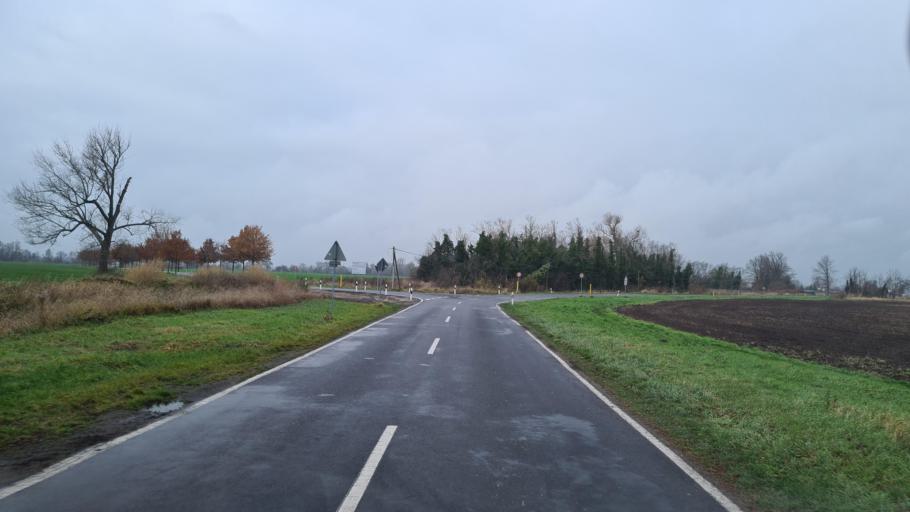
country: DE
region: Brandenburg
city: Nauen
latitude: 52.6250
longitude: 12.7940
